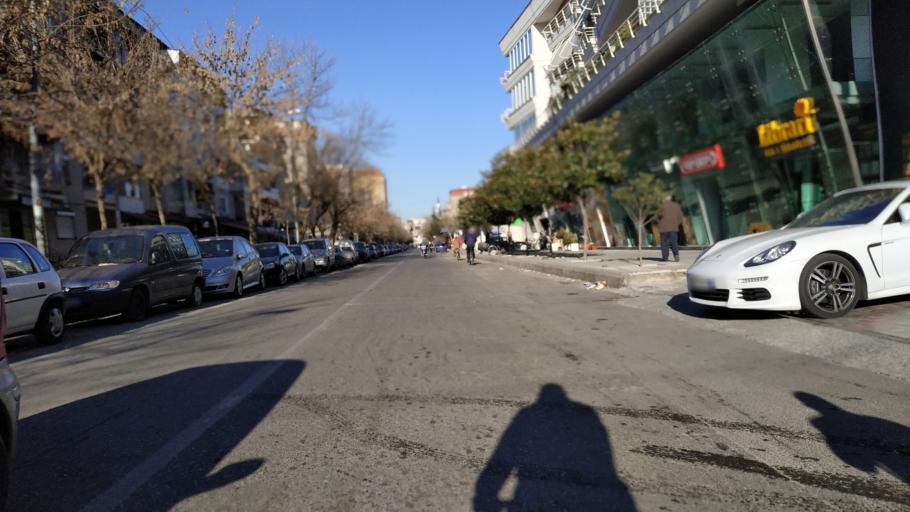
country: AL
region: Shkoder
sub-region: Rrethi i Shkodres
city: Shkoder
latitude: 42.0620
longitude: 19.5118
